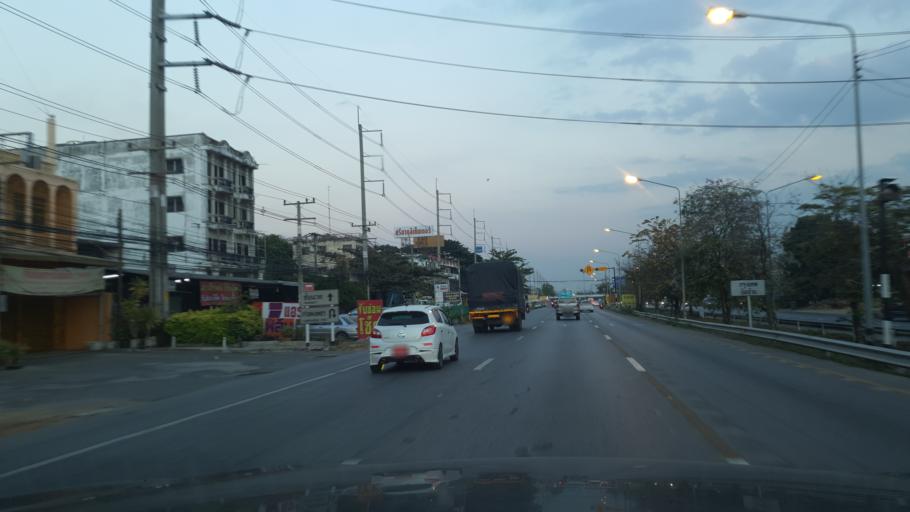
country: TH
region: Nakhon Sawan
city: Nakhon Sawan
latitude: 15.7070
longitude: 100.1030
